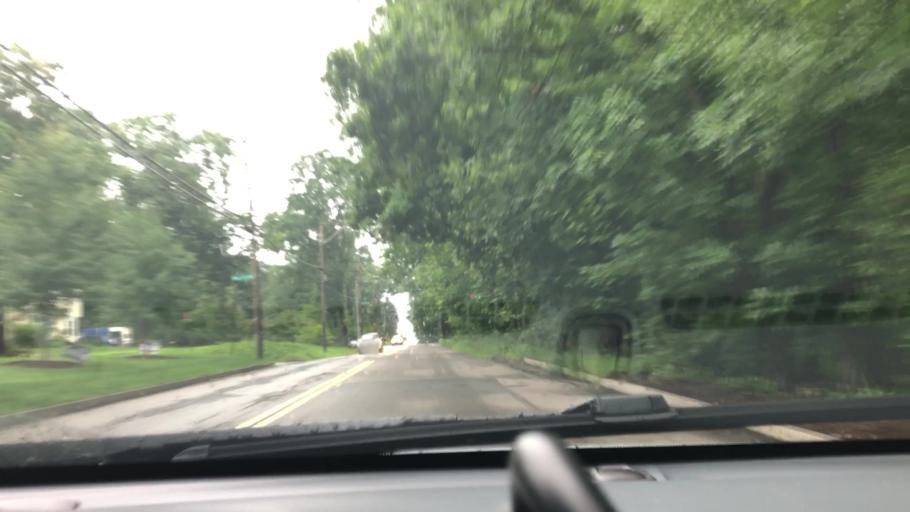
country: US
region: New Hampshire
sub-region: Merrimack County
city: South Hooksett
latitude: 43.0239
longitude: -71.4623
